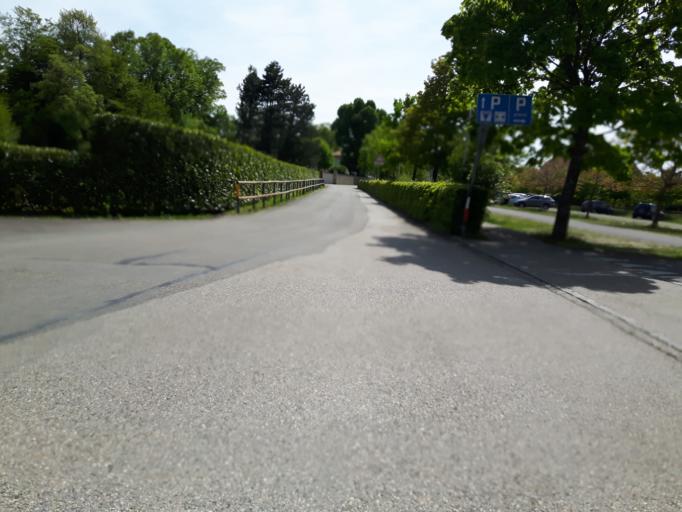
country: CH
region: Neuchatel
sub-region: Boudry District
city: Cortaillod
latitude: 46.9426
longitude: 6.8533
